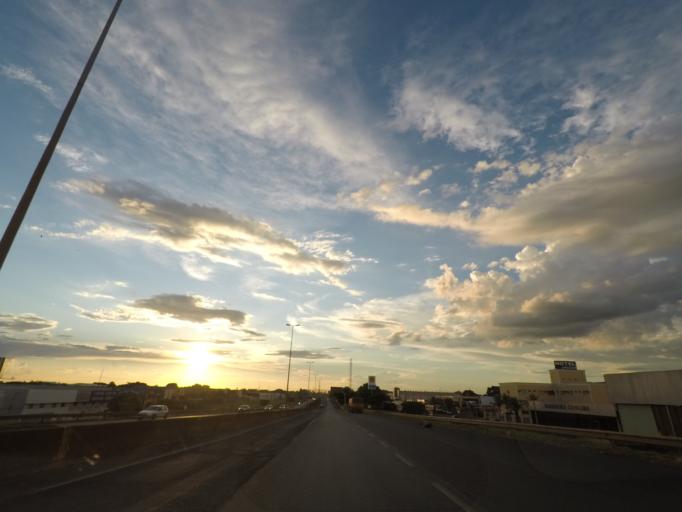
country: BR
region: Minas Gerais
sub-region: Uberaba
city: Uberaba
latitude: -19.7779
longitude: -47.9250
